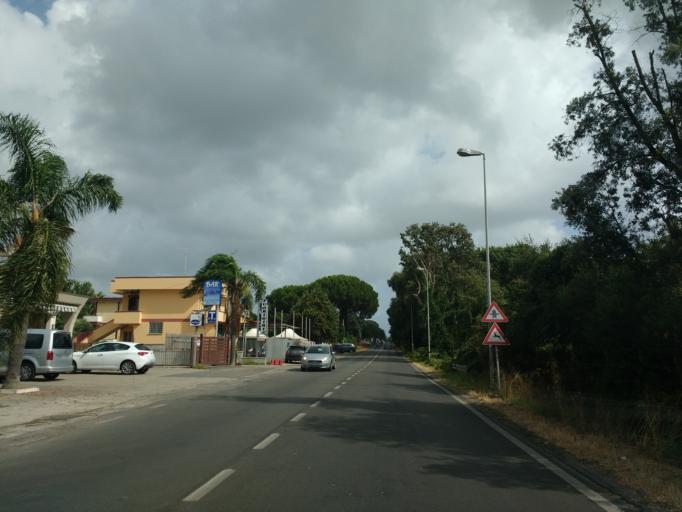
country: IT
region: Latium
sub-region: Citta metropolitana di Roma Capitale
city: Lavinio
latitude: 41.4903
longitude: 12.5967
